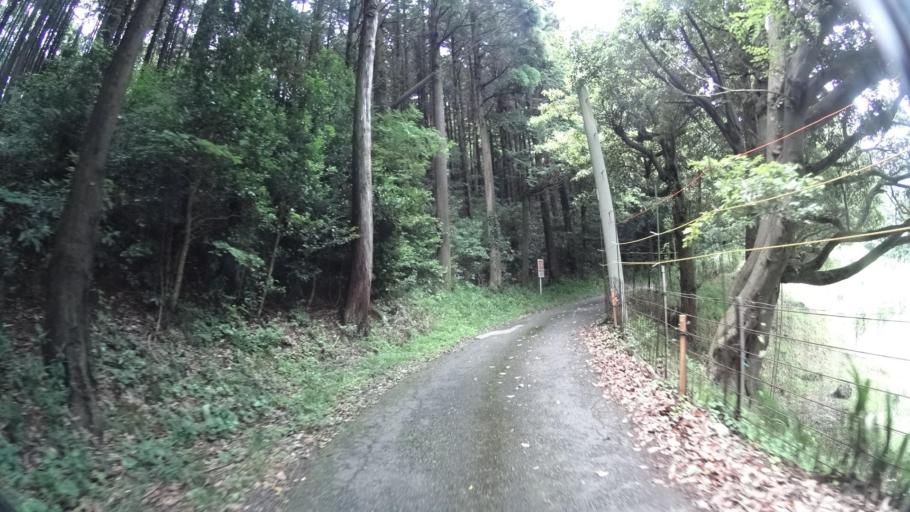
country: JP
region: Kyoto
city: Maizuru
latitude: 35.5316
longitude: 135.3411
